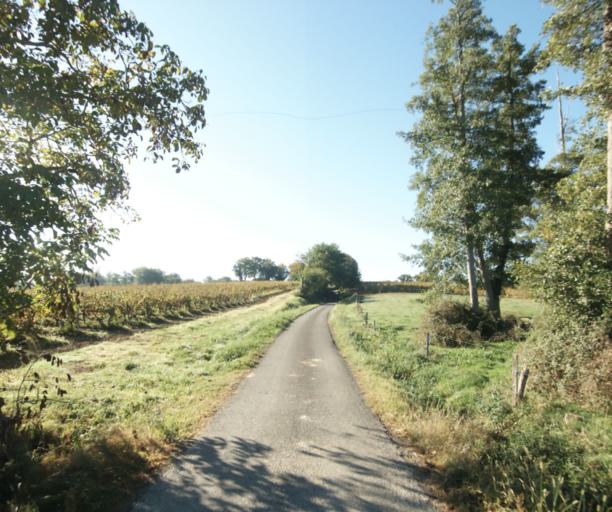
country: FR
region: Midi-Pyrenees
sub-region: Departement du Gers
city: Gondrin
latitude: 43.8452
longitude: 0.2330
